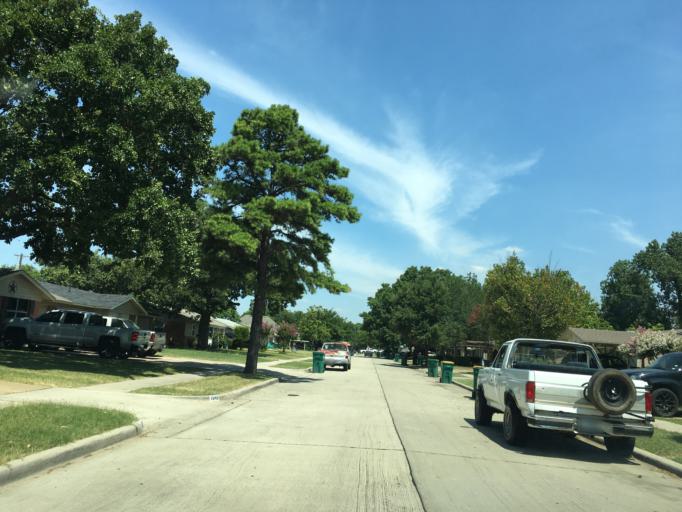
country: US
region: Texas
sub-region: Denton County
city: Lewisville
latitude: 33.0300
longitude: -96.9998
